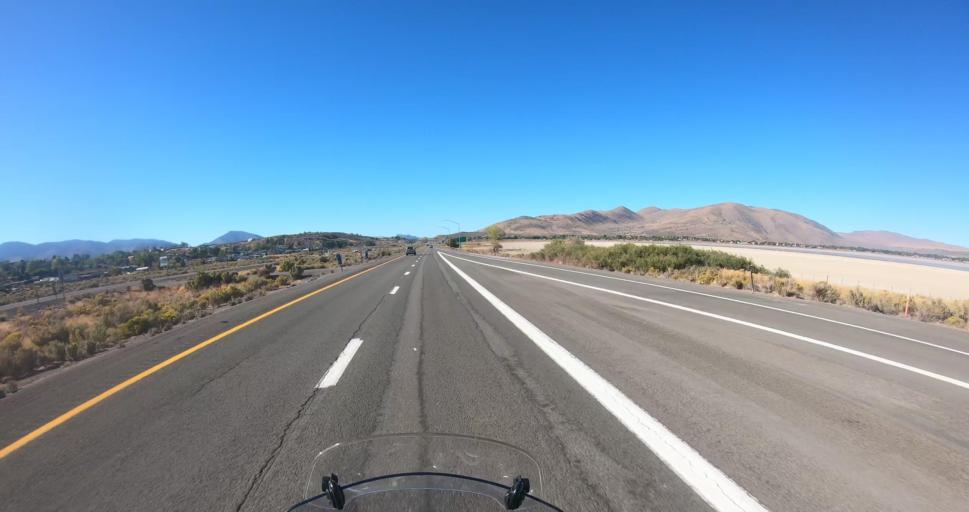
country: US
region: Nevada
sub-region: Washoe County
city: Cold Springs
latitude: 39.6563
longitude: -119.9855
